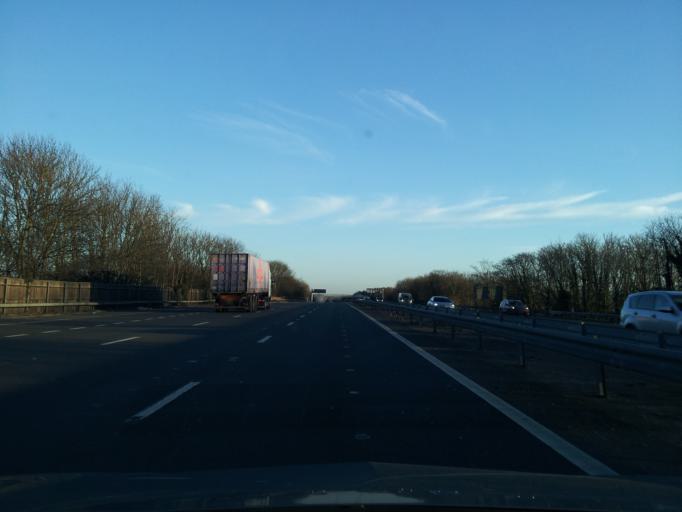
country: GB
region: England
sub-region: Milton Keynes
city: Newport Pagnell
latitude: 52.0816
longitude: -0.7455
